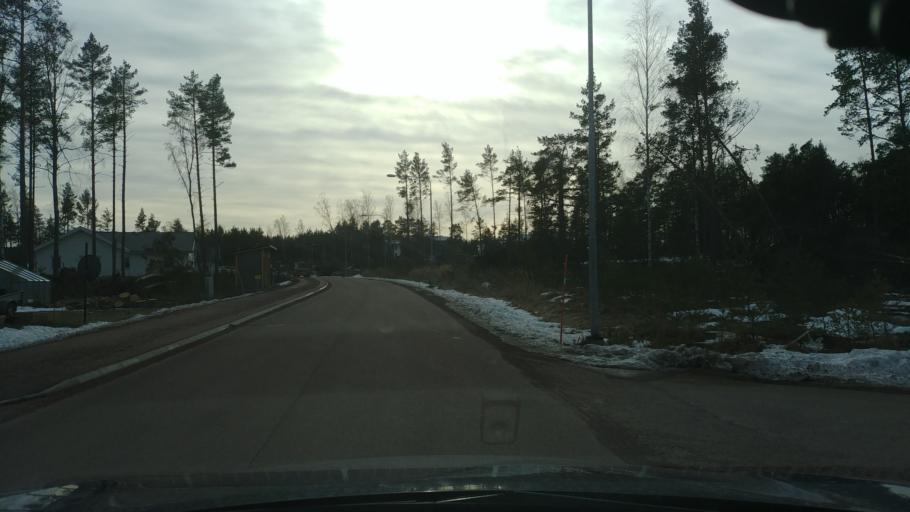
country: AX
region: Mariehamns stad
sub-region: Mariehamn
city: Mariehamn
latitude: 60.1016
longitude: 19.8928
